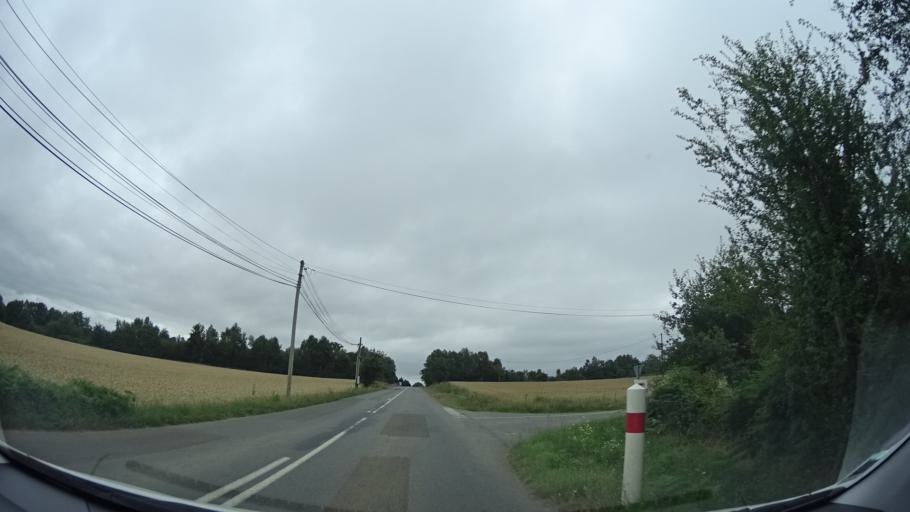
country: FR
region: Brittany
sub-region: Departement d'Ille-et-Vilaine
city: Saint-Domineuc
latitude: 48.3687
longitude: -1.8872
